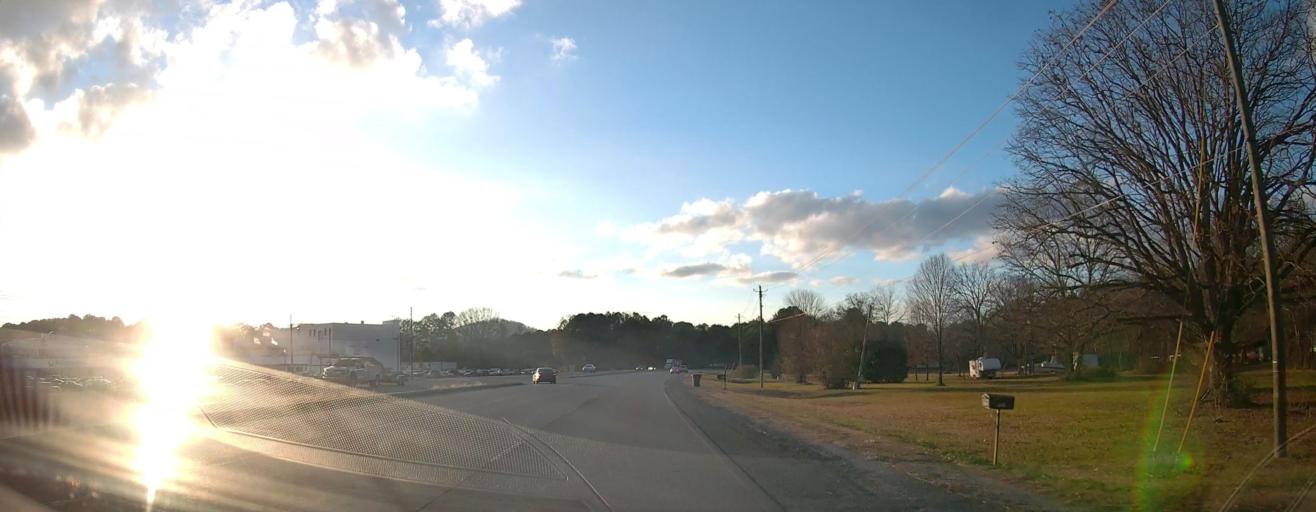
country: US
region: Alabama
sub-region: Etowah County
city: Glencoe
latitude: 33.9721
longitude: -85.9706
